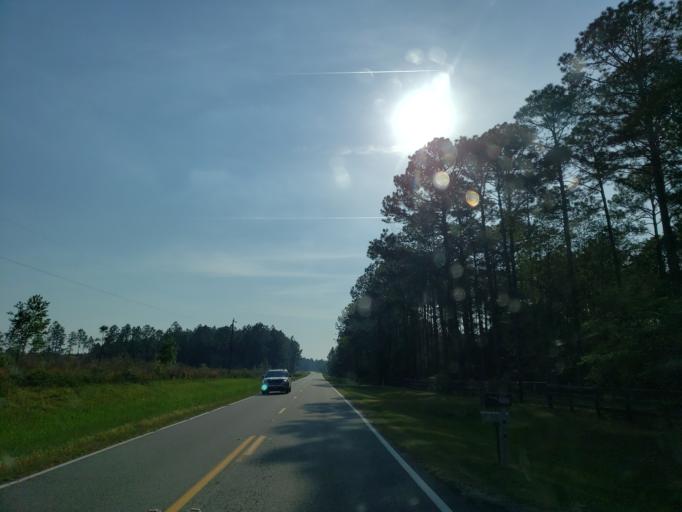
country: US
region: Georgia
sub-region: Tift County
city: Tifton
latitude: 31.5543
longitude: -83.5220
